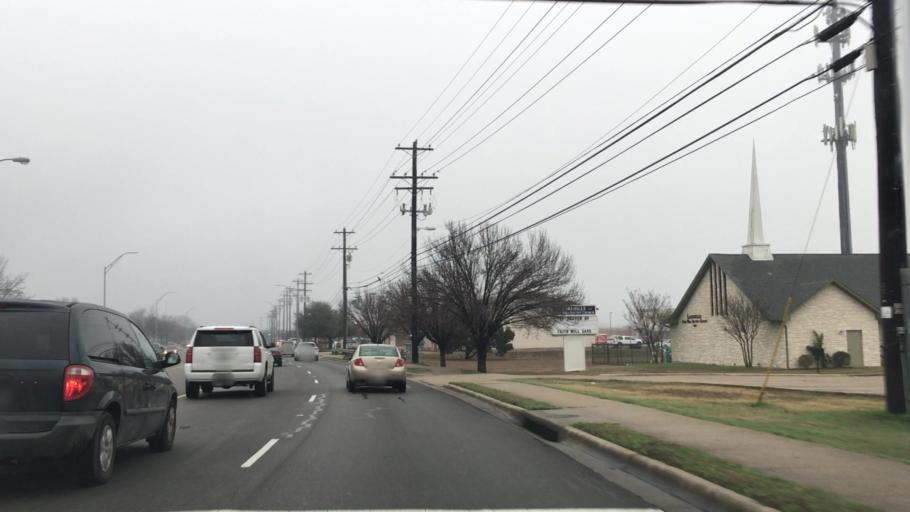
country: US
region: Texas
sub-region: Williamson County
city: Cedar Park
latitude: 30.4778
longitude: -97.8344
